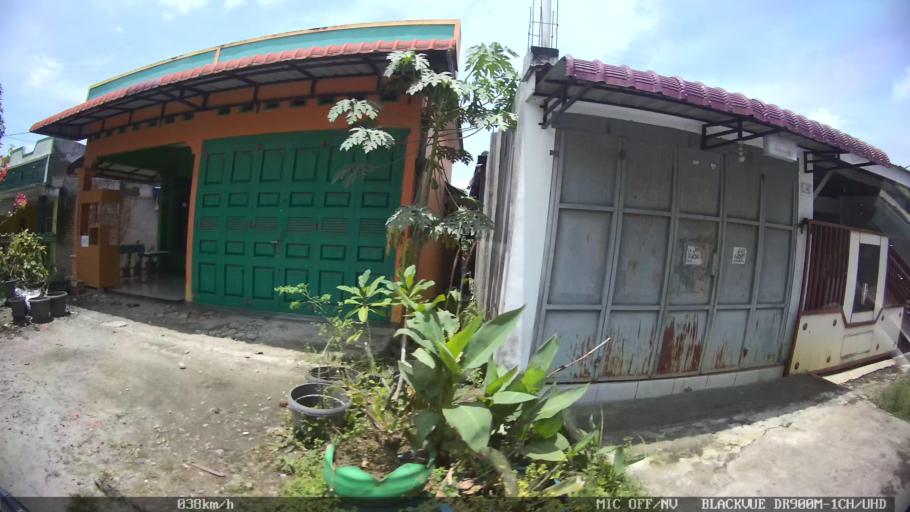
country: ID
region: North Sumatra
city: Percut
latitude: 3.5456
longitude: 98.8737
